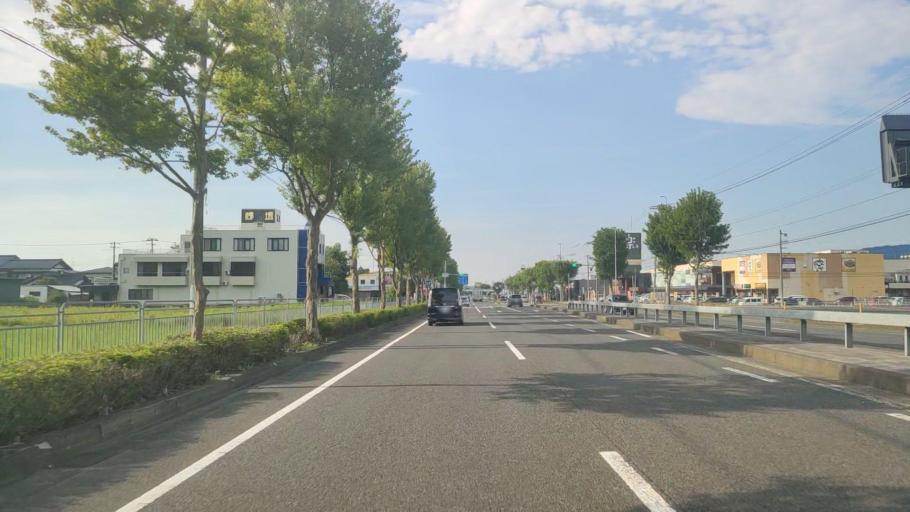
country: JP
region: Fukui
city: Takefu
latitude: 35.9051
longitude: 136.1921
